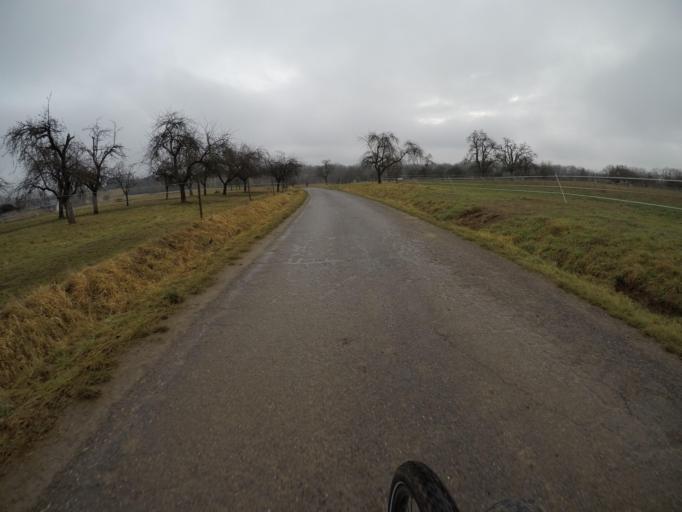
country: DE
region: Baden-Wuerttemberg
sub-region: Regierungsbezirk Stuttgart
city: Wolfschlugen
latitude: 48.6369
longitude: 9.2618
